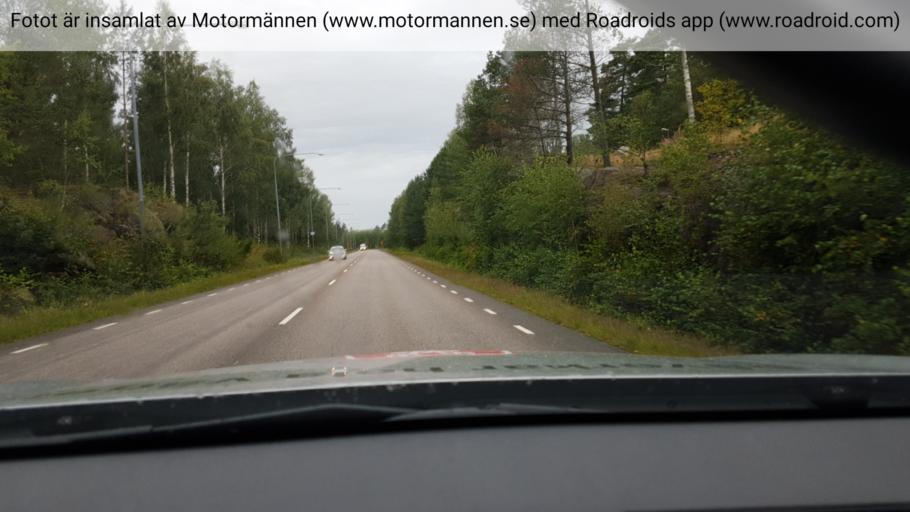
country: SE
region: Vaestra Goetaland
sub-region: Trollhattan
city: Trollhattan
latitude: 58.3131
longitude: 12.2755
